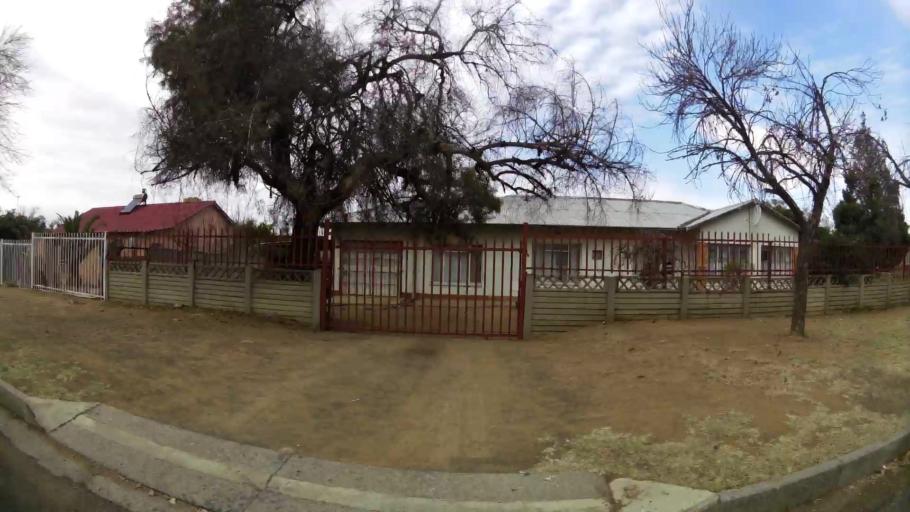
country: ZA
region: Orange Free State
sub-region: Fezile Dabi District Municipality
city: Kroonstad
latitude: -27.6349
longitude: 27.2253
